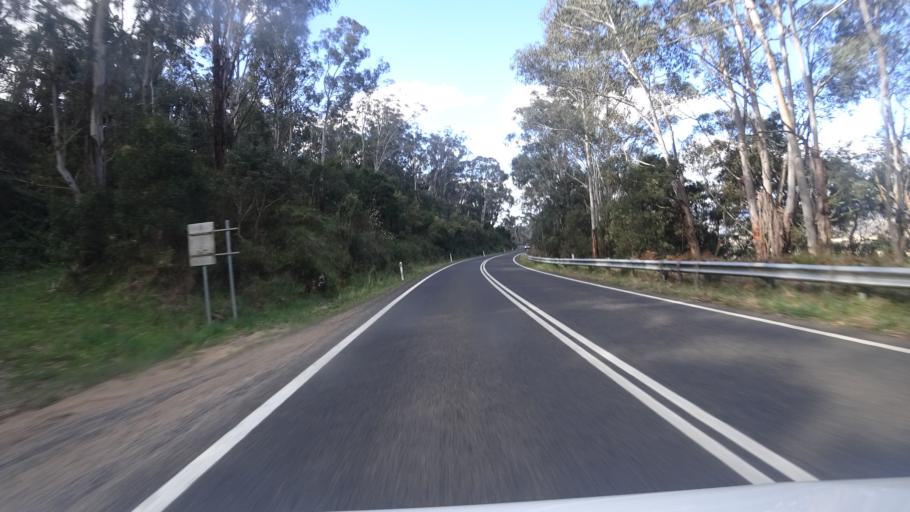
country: AU
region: New South Wales
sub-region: Lithgow
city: Bowenfels
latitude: -33.6652
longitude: 150.0494
